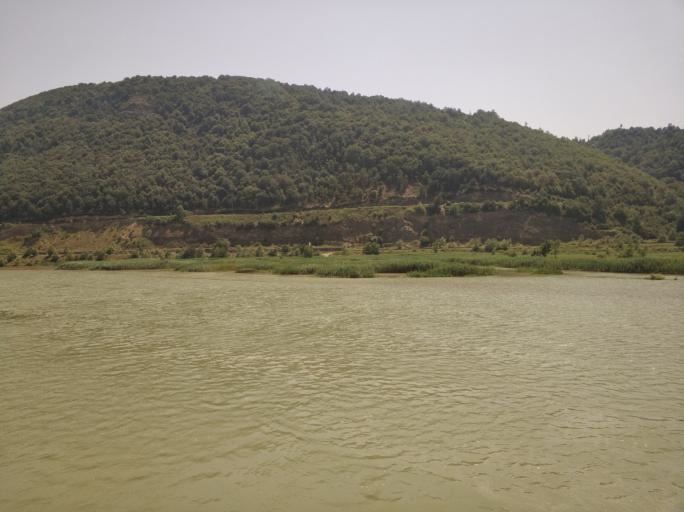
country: IR
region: Gilan
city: Pa'in-e Bazar-e Rudbar
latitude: 36.9761
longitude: 49.5540
